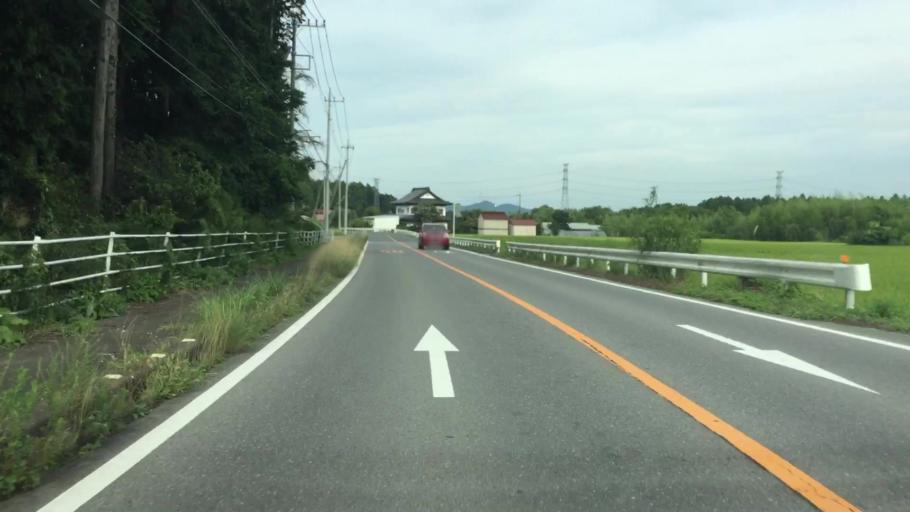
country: JP
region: Tochigi
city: Imaichi
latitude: 36.7439
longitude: 139.7412
